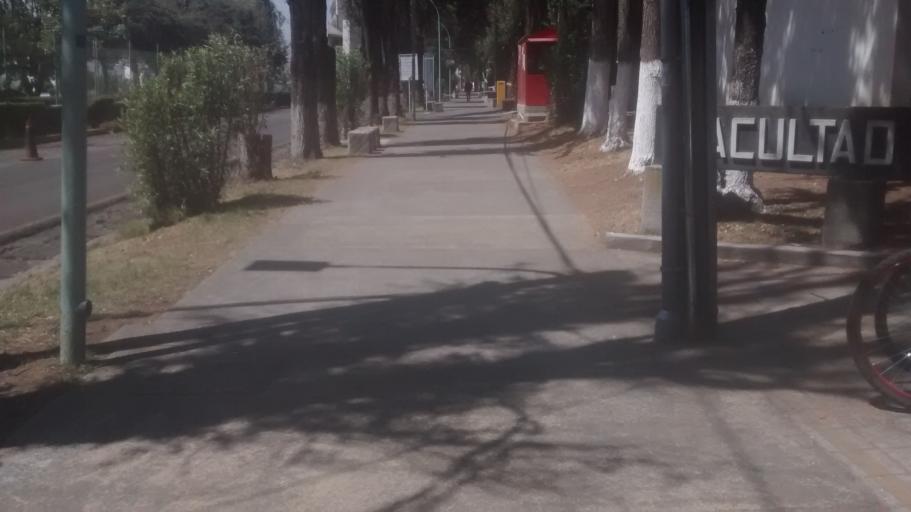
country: MX
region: Mexico
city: San Buenaventura
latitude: 19.2823
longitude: -99.6764
